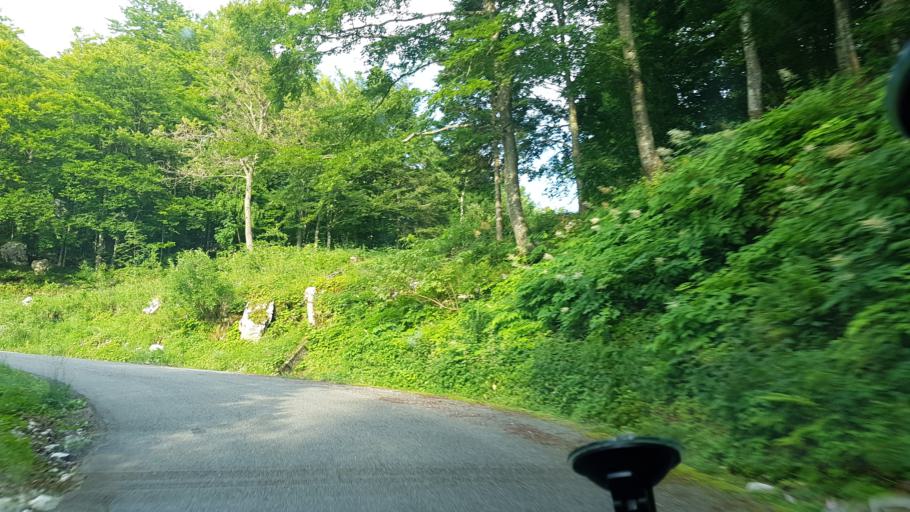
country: IT
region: Friuli Venezia Giulia
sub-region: Provincia di Udine
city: Prato
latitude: 46.3370
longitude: 13.3186
